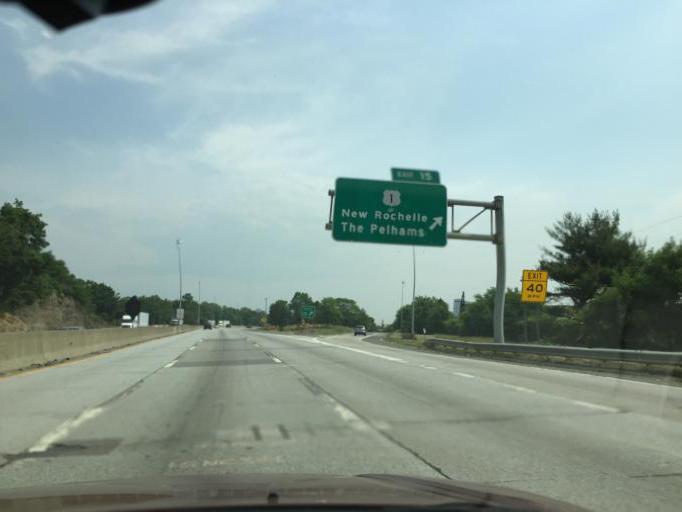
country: US
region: New York
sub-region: Westchester County
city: Pelham Manor
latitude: 40.8975
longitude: -73.7970
